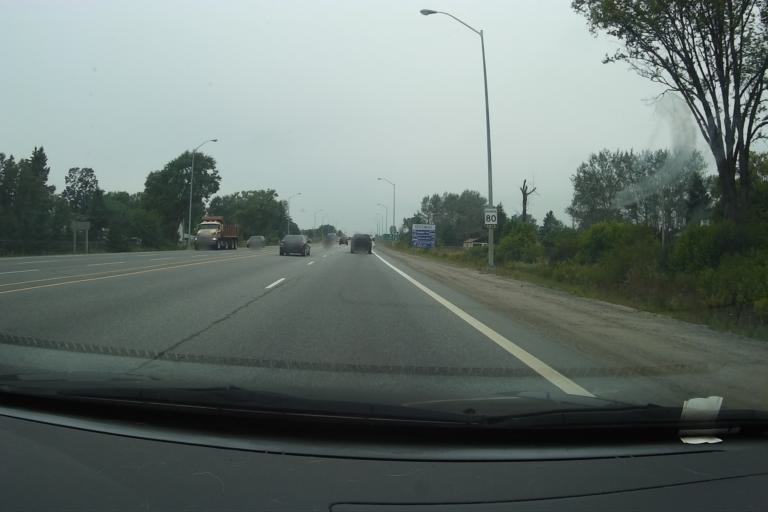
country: CA
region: Ontario
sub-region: Nipissing District
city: North Bay
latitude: 46.3284
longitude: -79.4589
